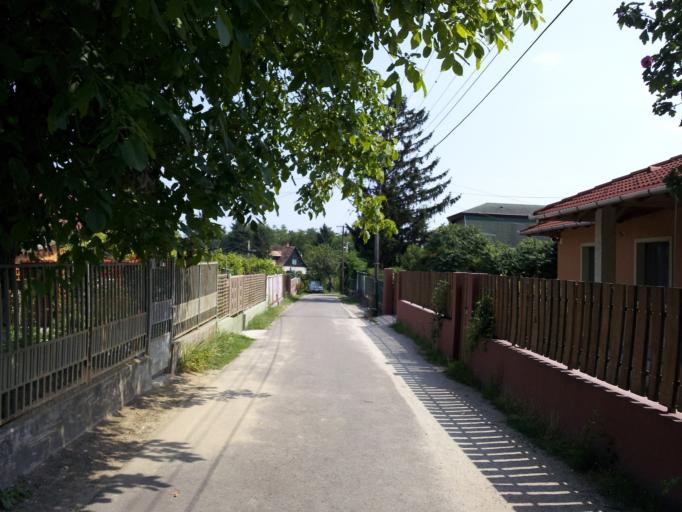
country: HU
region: Pest
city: Szigethalom
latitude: 47.3106
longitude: 19.0238
